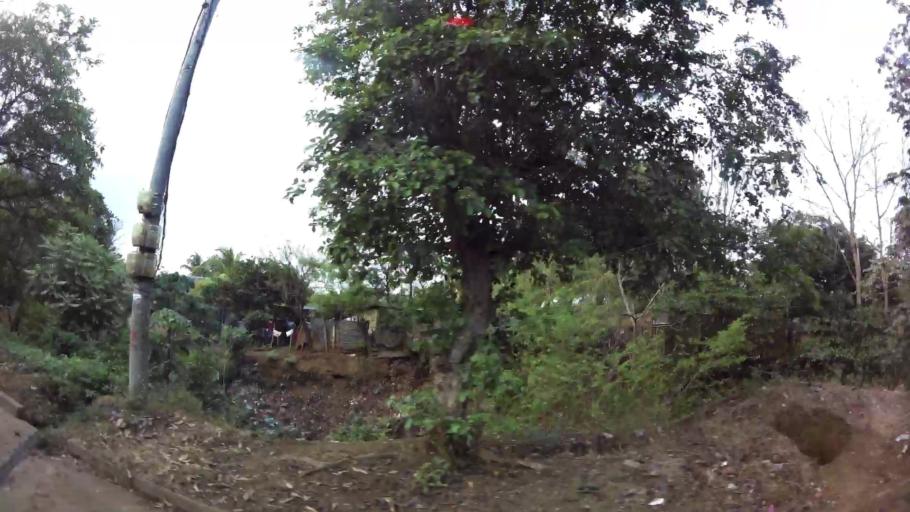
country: NI
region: Masaya
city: Masaya
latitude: 11.9871
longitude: -86.1055
